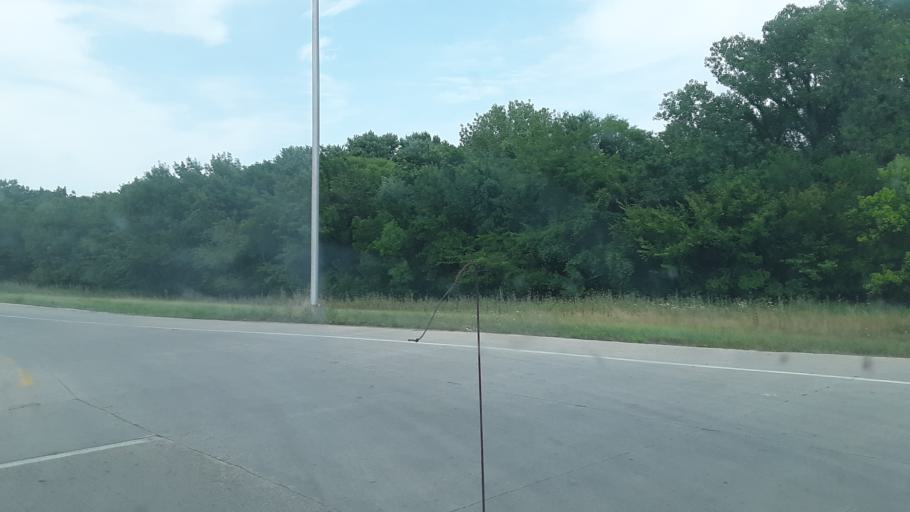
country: US
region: Kansas
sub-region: Bourbon County
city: Fort Scott
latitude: 37.8550
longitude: -94.7015
